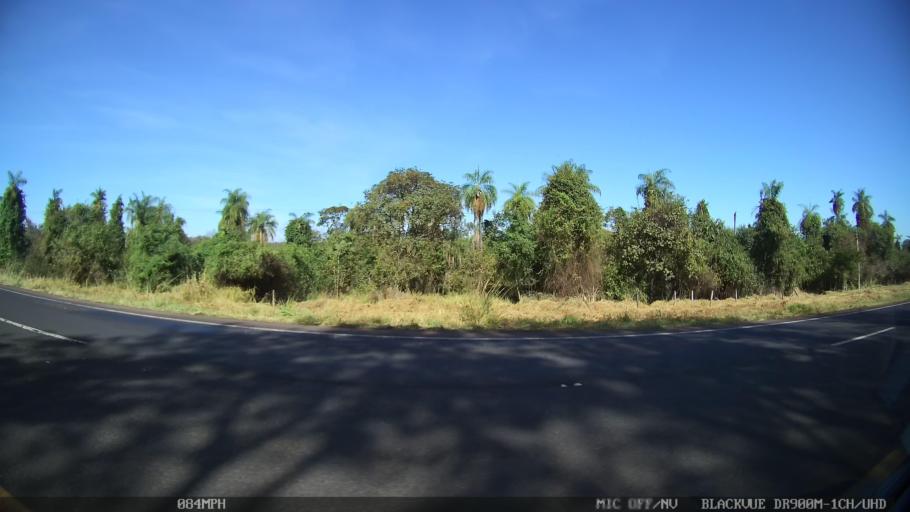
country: BR
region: Sao Paulo
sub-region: Barretos
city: Barretos
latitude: -20.5876
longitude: -48.7021
